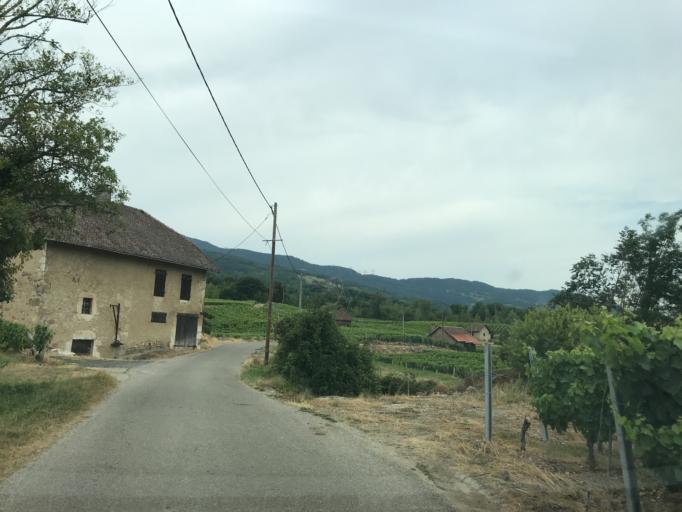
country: FR
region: Rhone-Alpes
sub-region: Departement de l'Isere
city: Chapareillan
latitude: 45.4877
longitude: 5.9667
